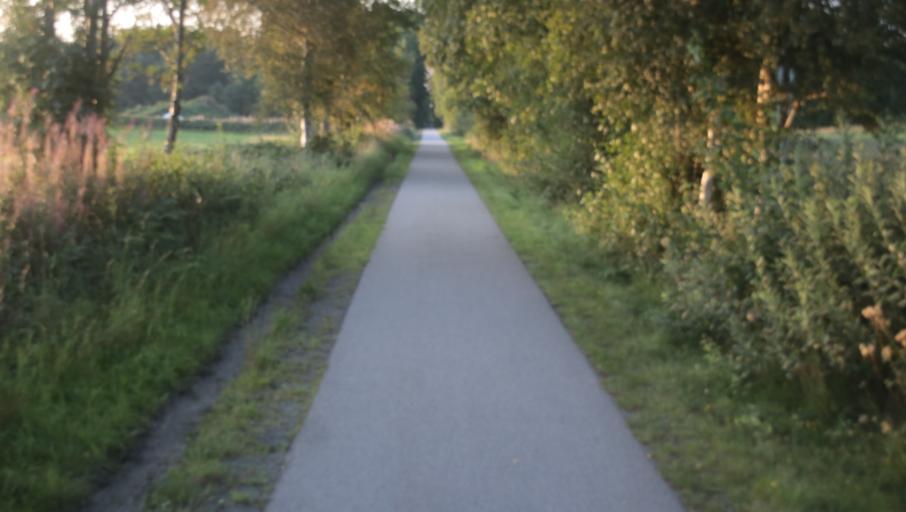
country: SE
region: Blekinge
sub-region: Karlshamns Kommun
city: Karlshamn
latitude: 56.2174
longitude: 14.8231
